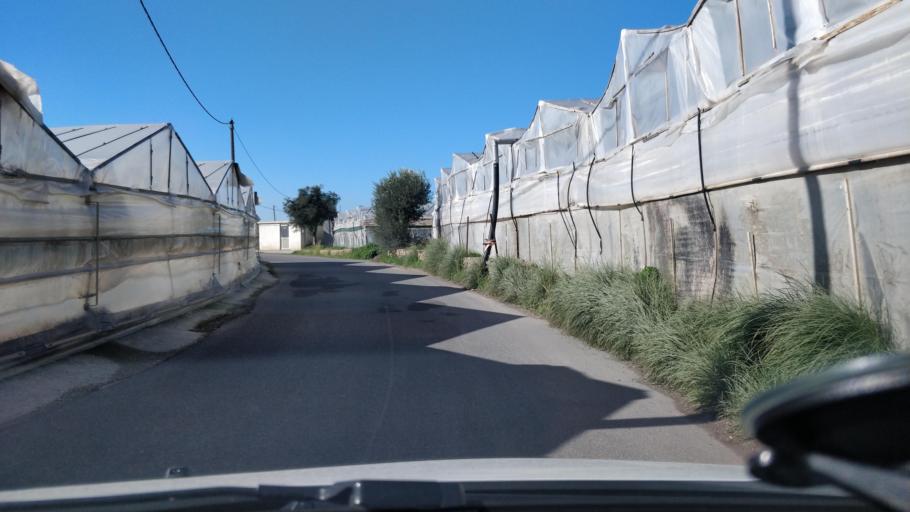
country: GR
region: Crete
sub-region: Nomos Lasithiou
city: Gra Liyia
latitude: 35.0183
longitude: 25.6770
